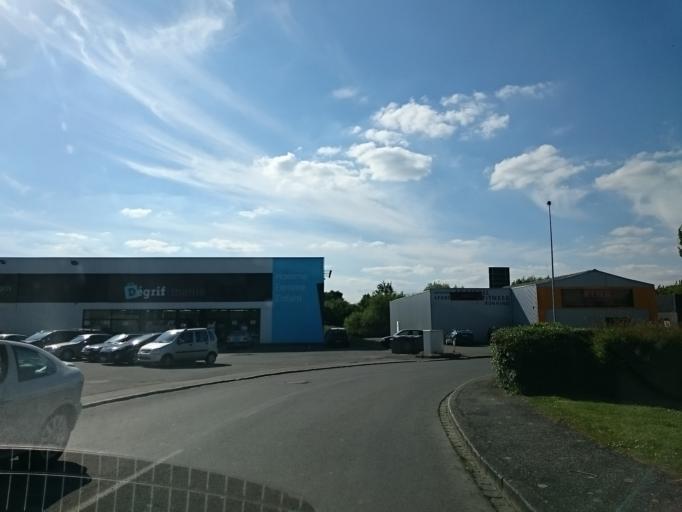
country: FR
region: Brittany
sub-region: Departement d'Ille-et-Vilaine
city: Chantepie
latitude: 48.0884
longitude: -1.6273
